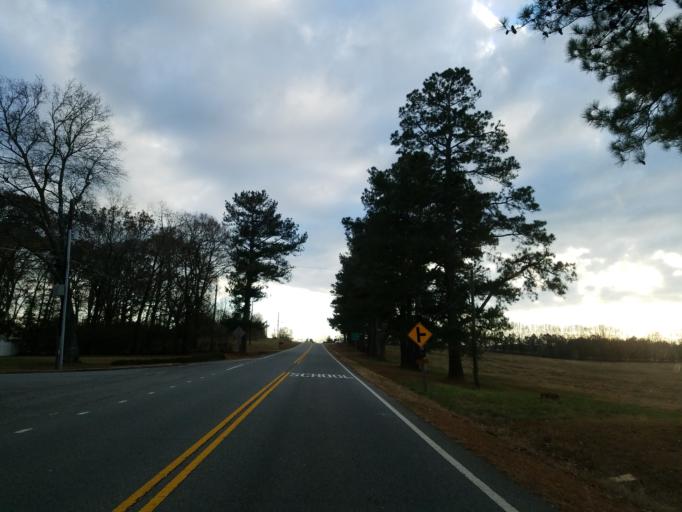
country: US
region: Georgia
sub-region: Forsyth County
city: Cumming
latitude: 34.2771
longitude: -84.0985
